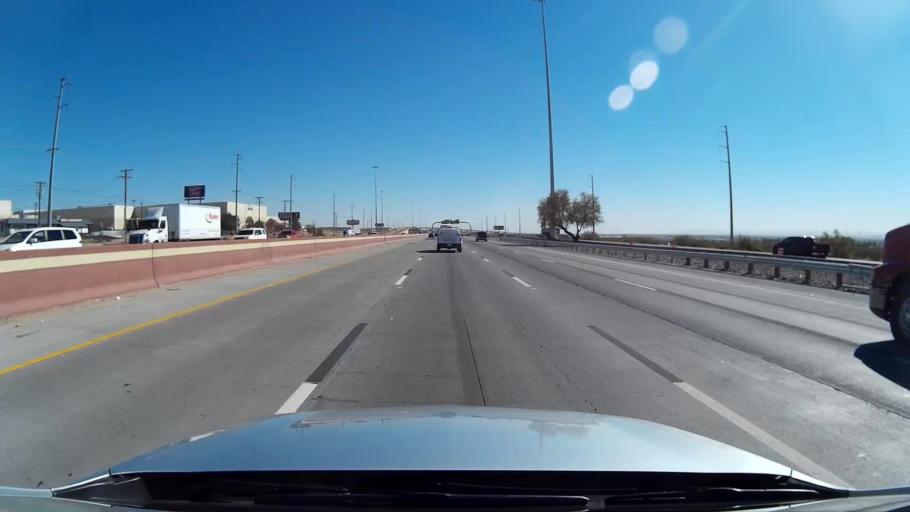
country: US
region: Texas
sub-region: El Paso County
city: Socorro
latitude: 31.7177
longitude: -106.3020
